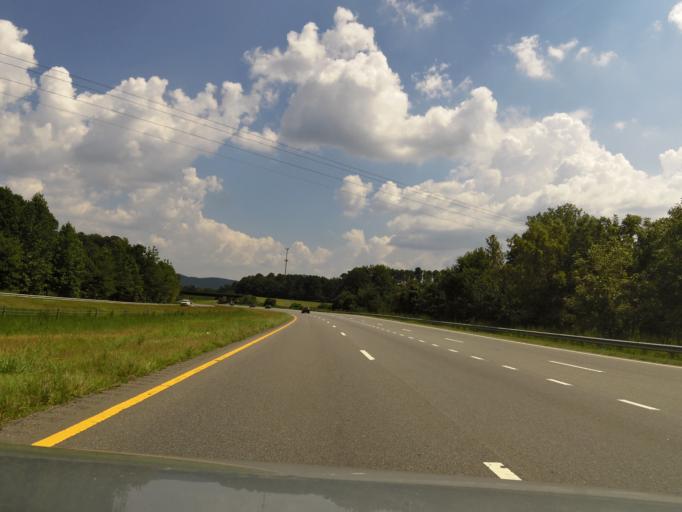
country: US
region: North Carolina
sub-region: Cleveland County
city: Kings Mountain
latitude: 35.2444
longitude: -81.3261
